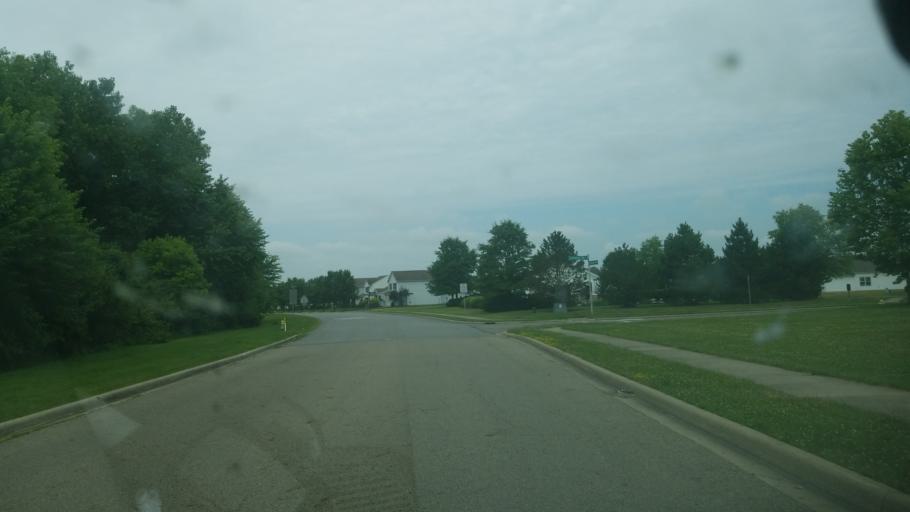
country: US
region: Ohio
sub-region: Franklin County
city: Reynoldsburg
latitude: 40.0118
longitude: -82.7822
